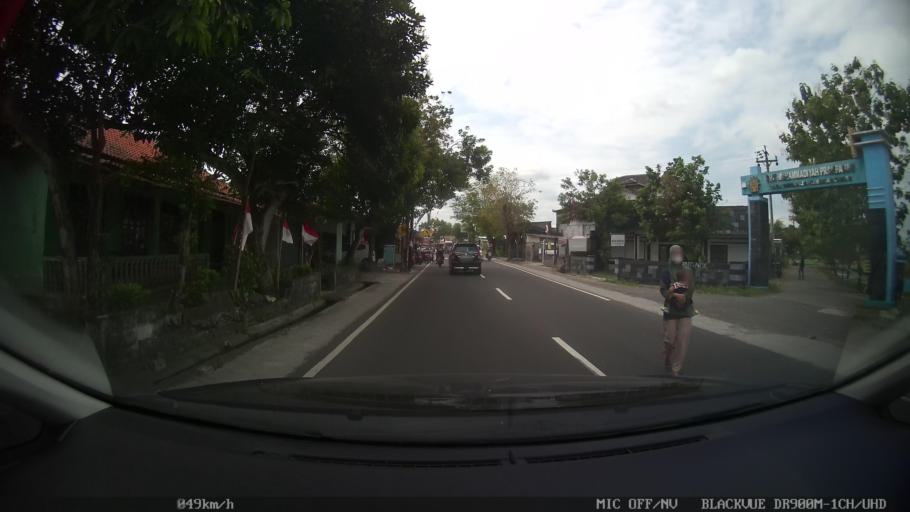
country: ID
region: Central Java
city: Candi Prambanan
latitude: -7.7655
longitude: 110.4881
